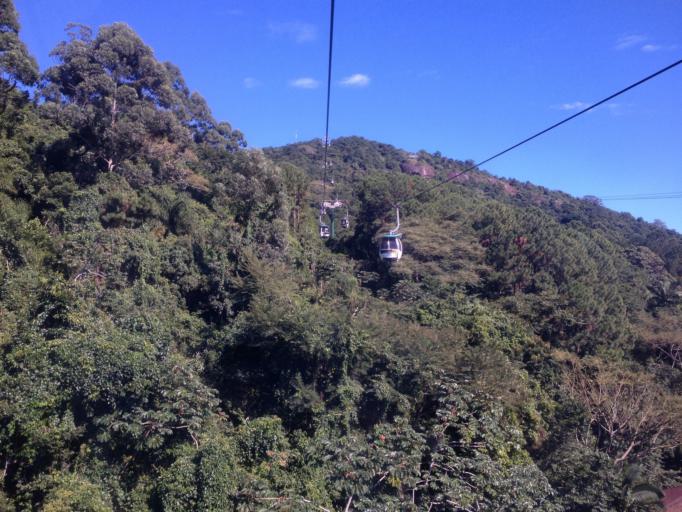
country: BR
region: Santa Catarina
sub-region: Balneario Camboriu
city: Balneario Camboriu
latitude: -26.9988
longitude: -48.5910
